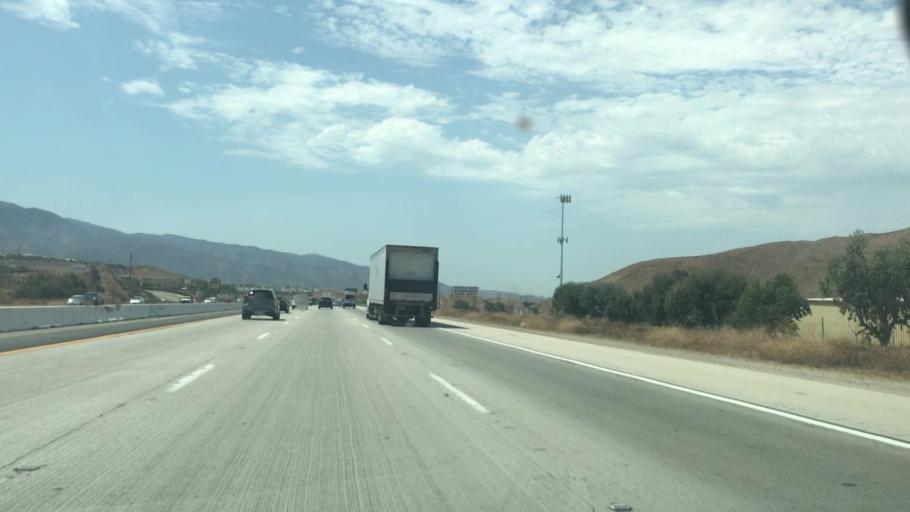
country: US
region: California
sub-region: Riverside County
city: El Cerrito
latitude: 33.7448
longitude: -117.4441
